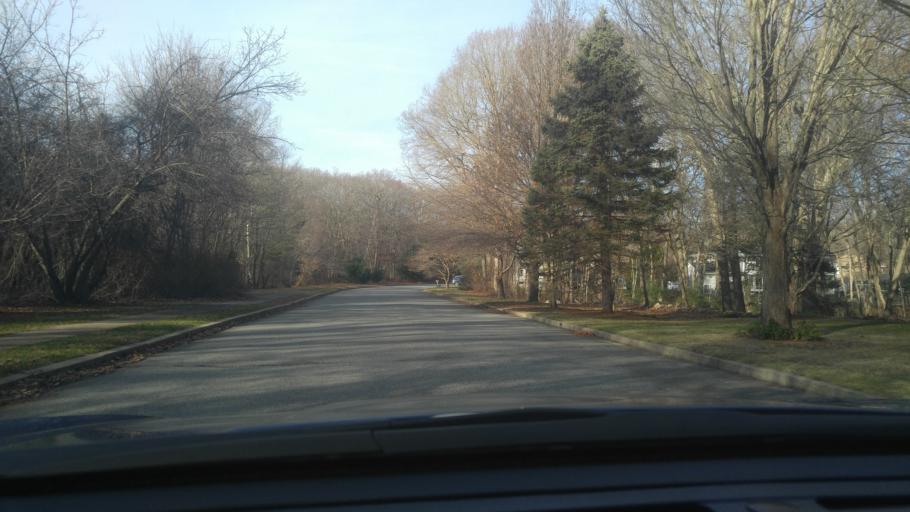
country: US
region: Rhode Island
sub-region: Kent County
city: East Greenwich
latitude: 41.6804
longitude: -71.4723
